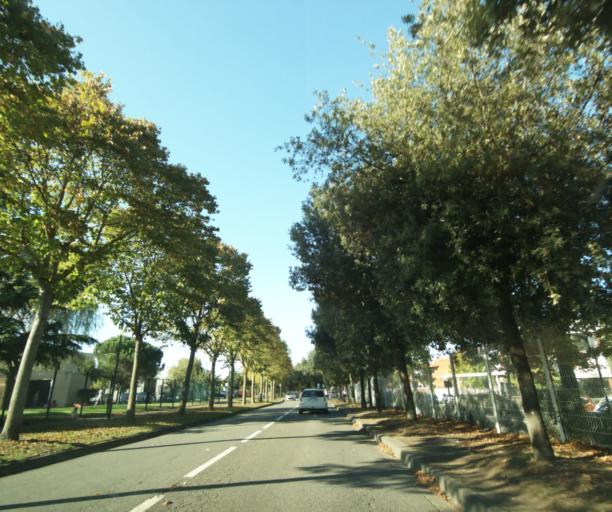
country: FR
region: Midi-Pyrenees
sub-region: Departement de la Haute-Garonne
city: Balma
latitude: 43.5820
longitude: 1.4940
